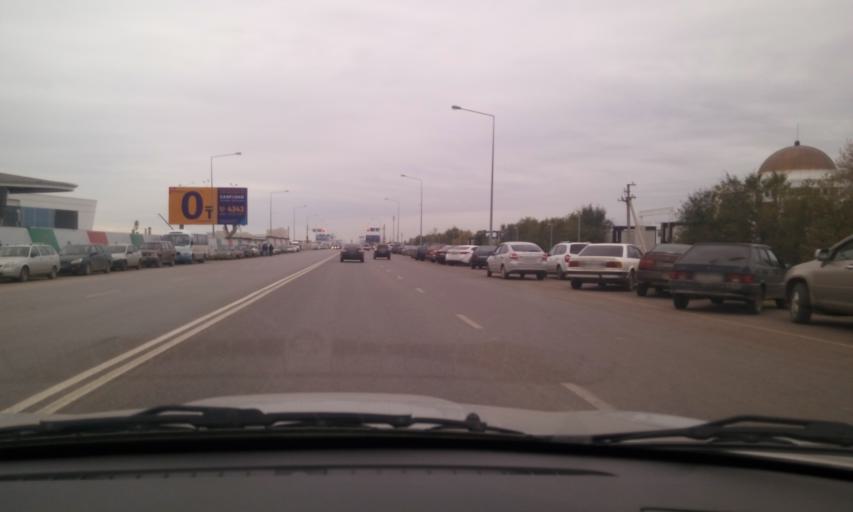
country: KZ
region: Astana Qalasy
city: Astana
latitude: 51.0917
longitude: 71.4034
